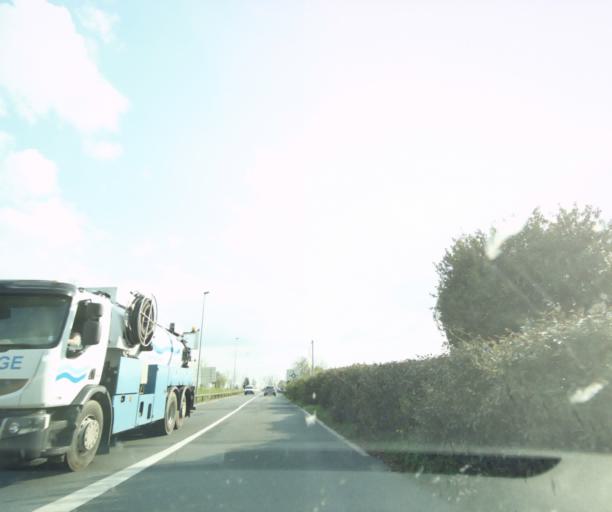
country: FR
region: Bourgogne
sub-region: Departement de Saone-et-Loire
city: Paray-le-Monial
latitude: 46.4676
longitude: 4.1182
